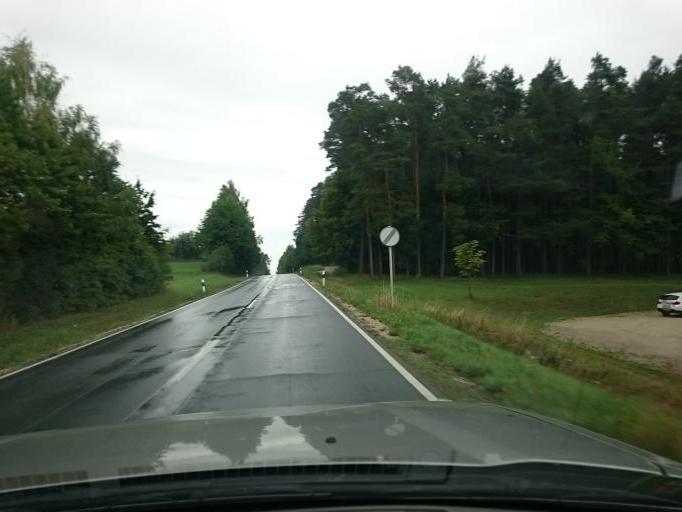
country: DE
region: Bavaria
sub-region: Upper Franconia
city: Pottenstein
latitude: 49.7512
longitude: 11.4045
